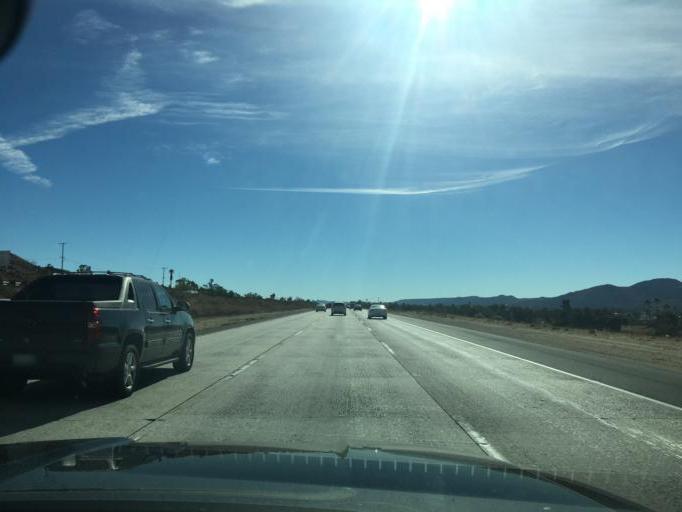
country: US
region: California
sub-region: Riverside County
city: Sedco Hills
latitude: 33.6471
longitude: -117.2873
